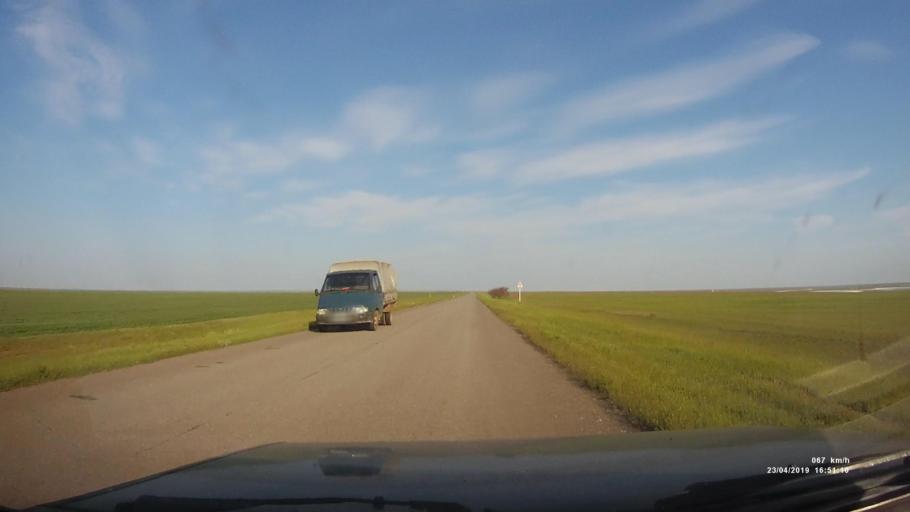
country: RU
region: Kalmykiya
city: Priyutnoye
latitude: 46.3241
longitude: 43.3022
